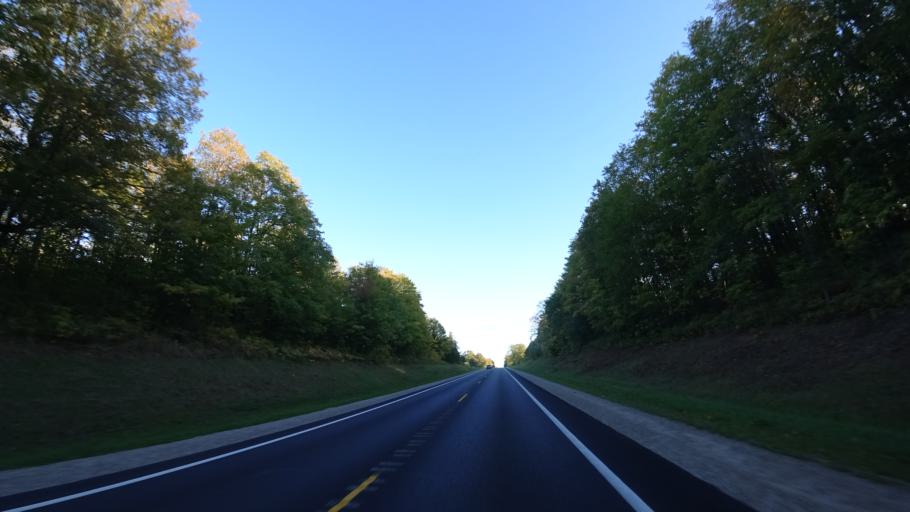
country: US
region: Michigan
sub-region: Luce County
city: Newberry
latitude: 46.3273
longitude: -85.6729
